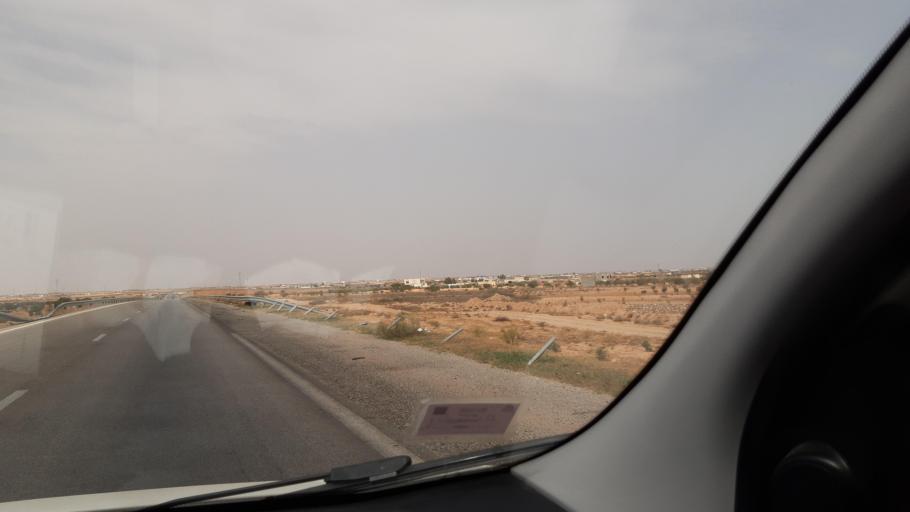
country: TN
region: Safaqis
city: Sfax
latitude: 34.7612
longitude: 10.6077
